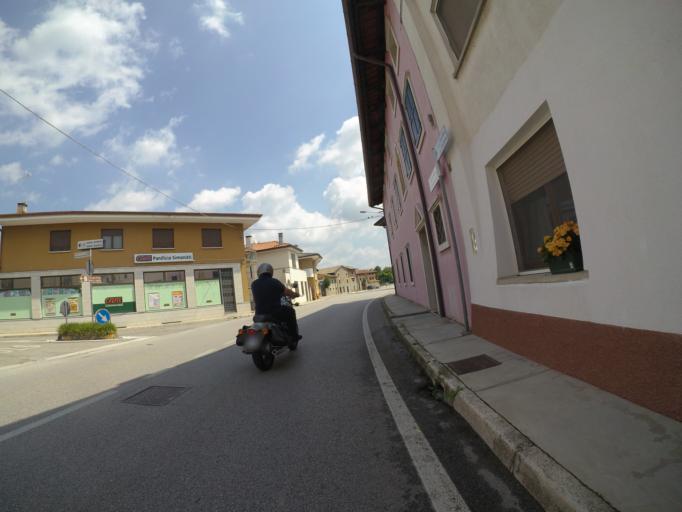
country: IT
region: Friuli Venezia Giulia
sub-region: Provincia di Udine
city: Mereto di Tomba
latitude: 46.0225
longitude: 13.0335
